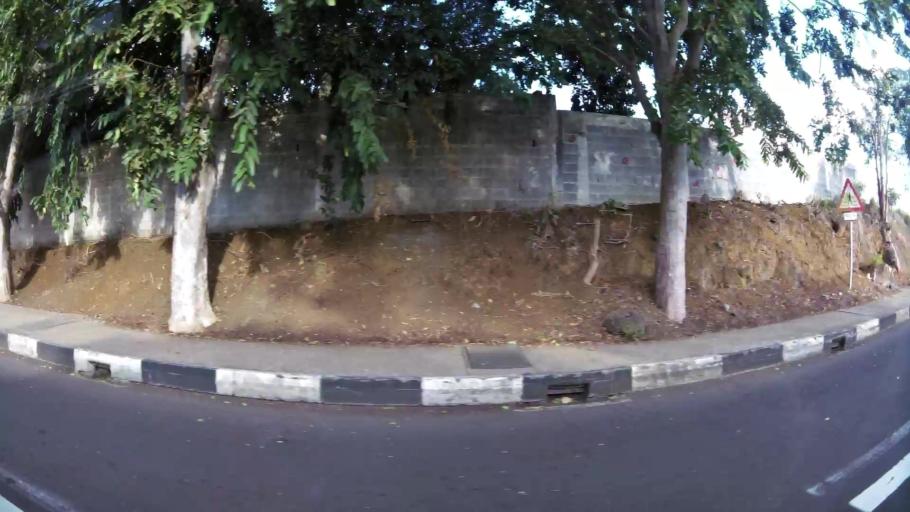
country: MU
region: Plaines Wilhems
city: Quatre Bornes
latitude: -20.2586
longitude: 57.4853
